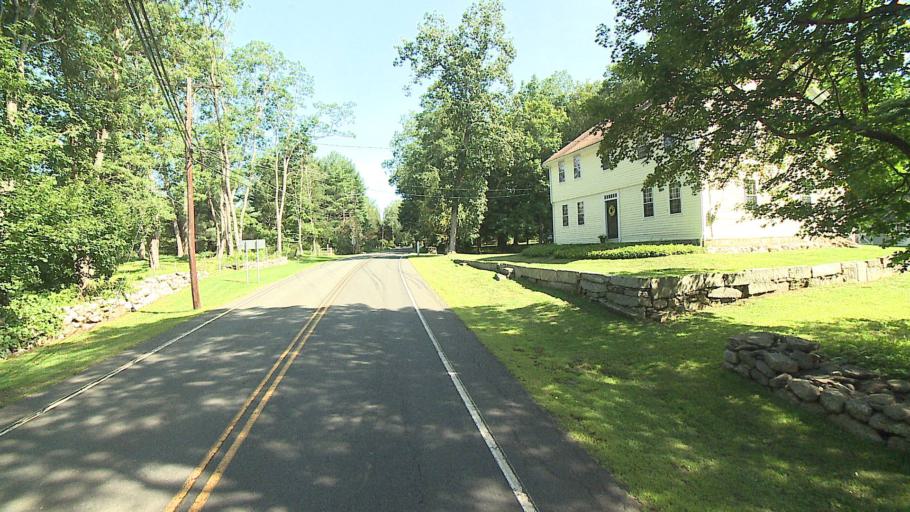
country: US
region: Connecticut
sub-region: Hartford County
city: West Simsbury
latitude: 41.8950
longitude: -72.8908
